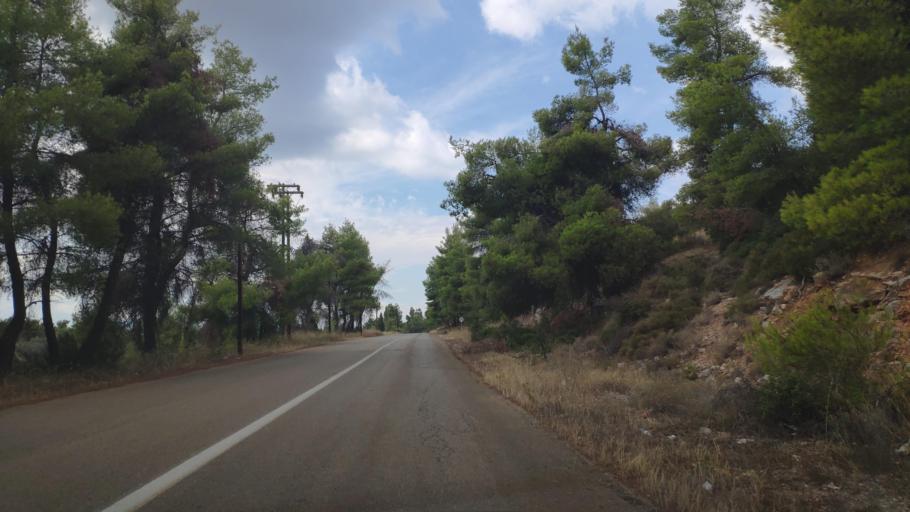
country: GR
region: Central Greece
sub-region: Nomos Fthiotidos
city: Malesina
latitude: 38.6387
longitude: 23.1898
